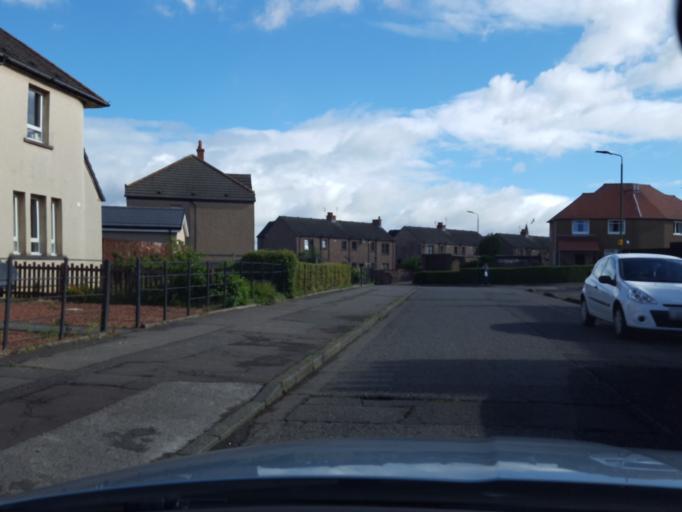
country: GB
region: Scotland
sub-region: Falkirk
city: Bo'ness
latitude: 56.0111
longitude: -3.6199
